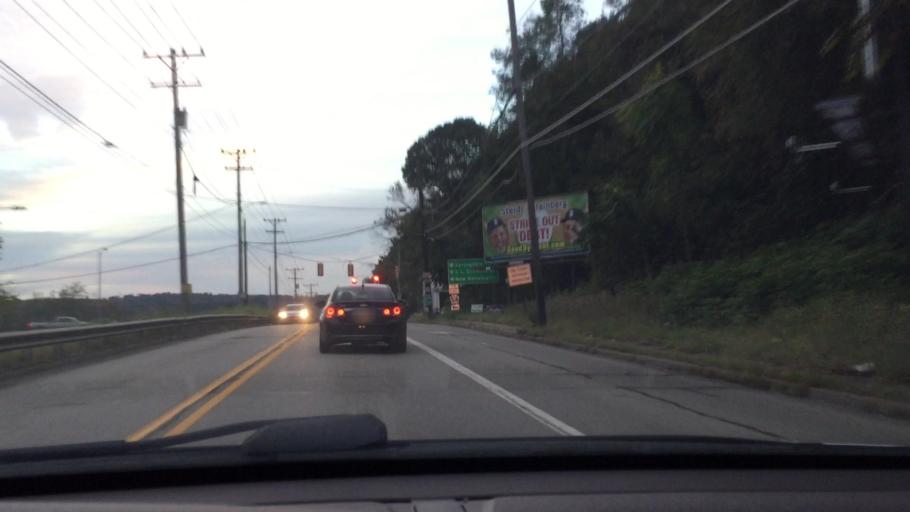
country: US
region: Pennsylvania
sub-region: Westmoreland County
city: New Kensington
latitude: 40.5645
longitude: -79.7748
